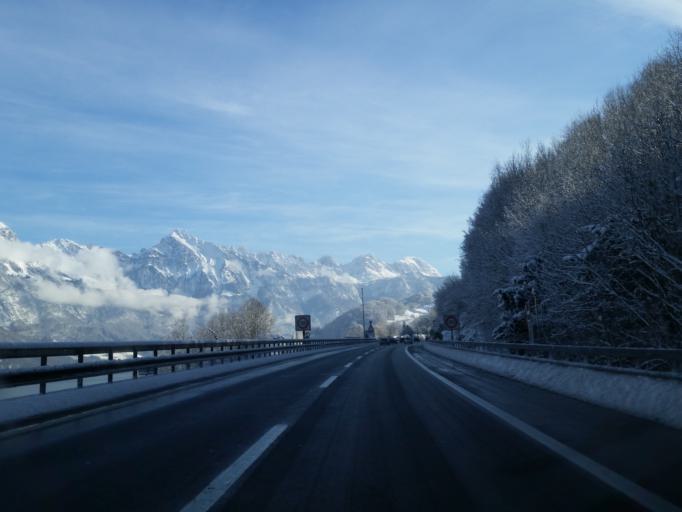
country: CH
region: Saint Gallen
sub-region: Wahlkreis Sarganserland
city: Quarten
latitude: 47.1105
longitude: 9.2299
